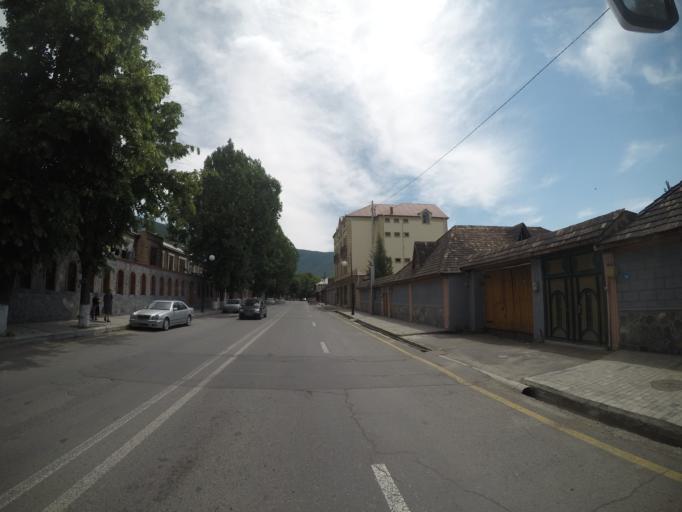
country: AZ
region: Shaki City
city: Sheki
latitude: 41.2060
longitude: 47.1728
